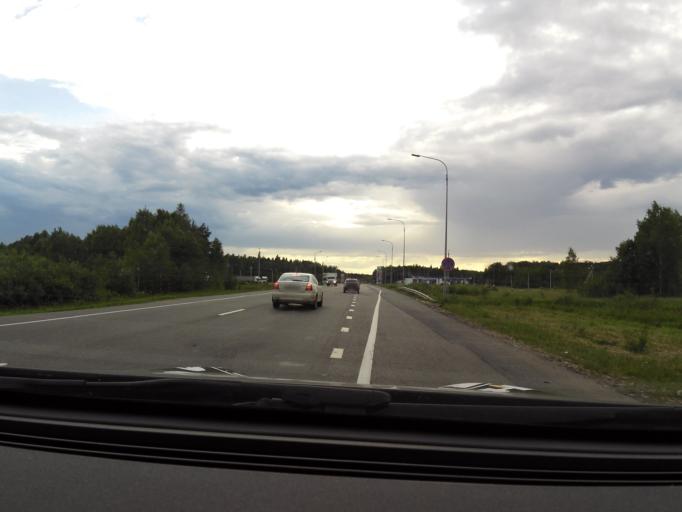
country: RU
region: Vladimir
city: Raduzhnyy
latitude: 56.0717
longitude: 40.2461
